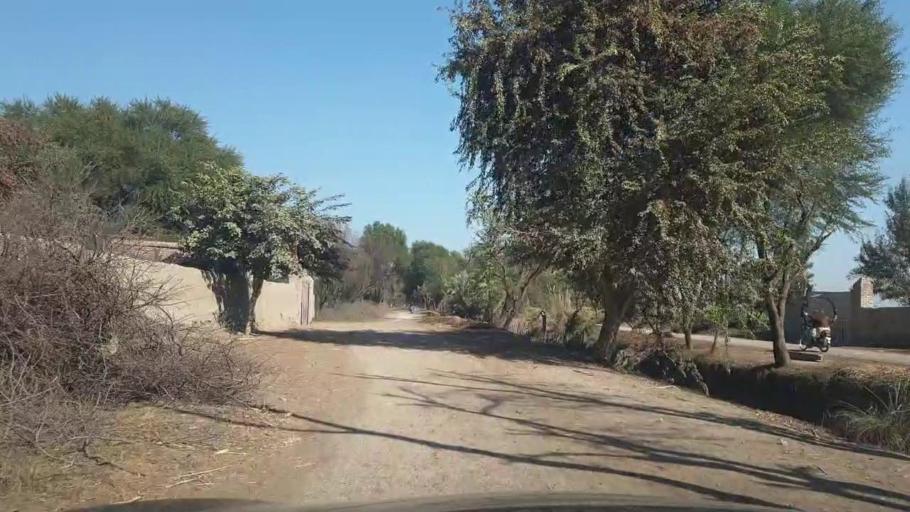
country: PK
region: Sindh
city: Ghotki
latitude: 27.9801
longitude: 69.4226
